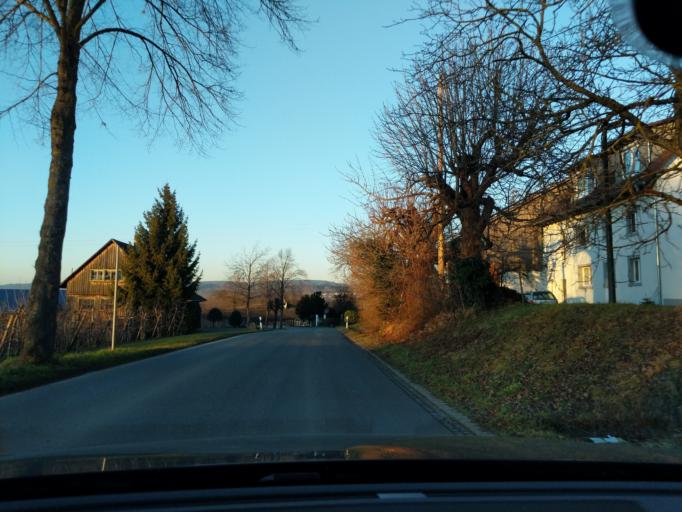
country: DE
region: Baden-Wuerttemberg
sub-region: Tuebingen Region
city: Hagnau
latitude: 47.7021
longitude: 9.3390
